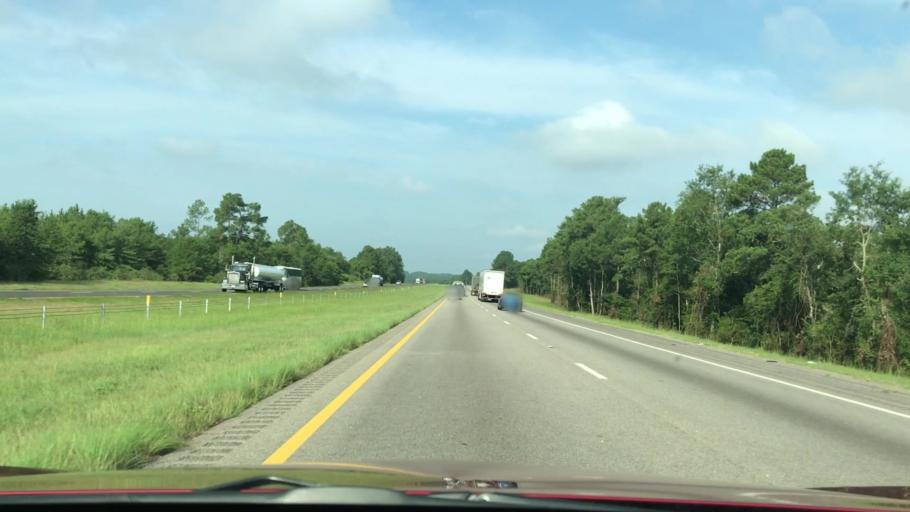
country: US
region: South Carolina
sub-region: Aiken County
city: Aiken
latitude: 33.6564
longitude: -81.6985
